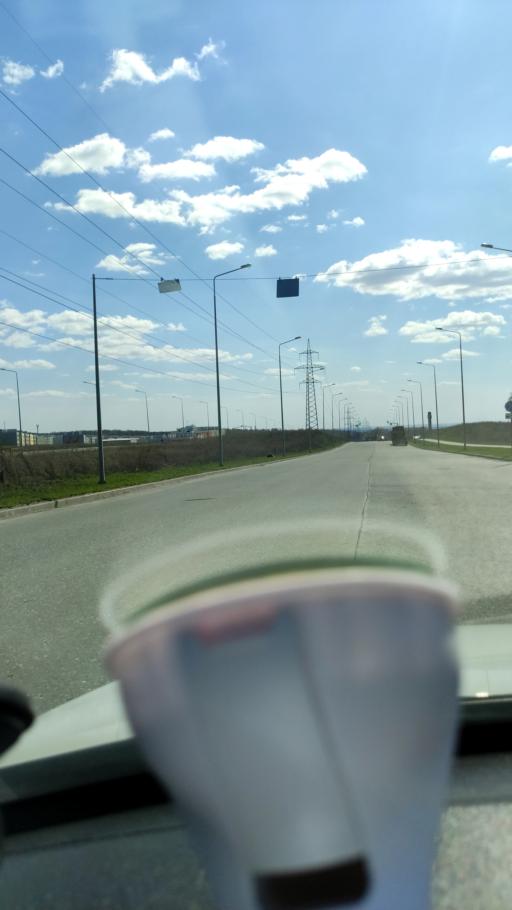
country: RU
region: Samara
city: Petra-Dubrava
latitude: 53.3088
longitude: 50.3379
